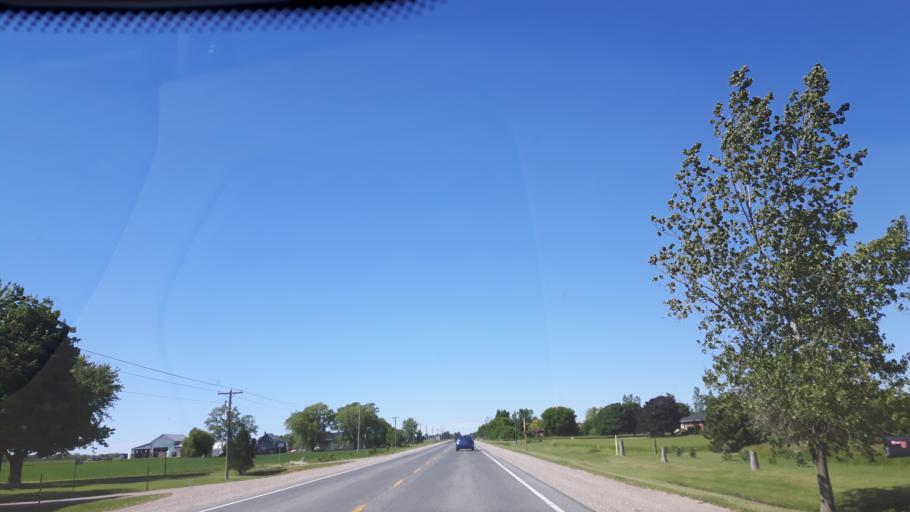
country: CA
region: Ontario
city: Bluewater
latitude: 43.4255
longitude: -81.7045
